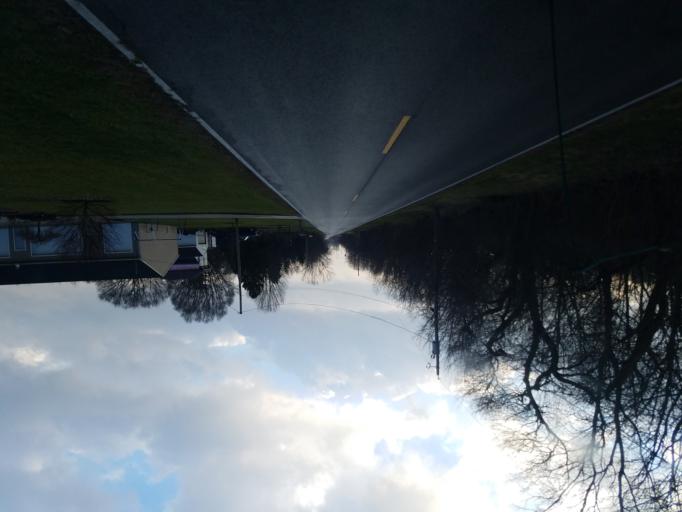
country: US
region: Ohio
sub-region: Marion County
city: Marion
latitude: 40.6053
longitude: -83.1548
